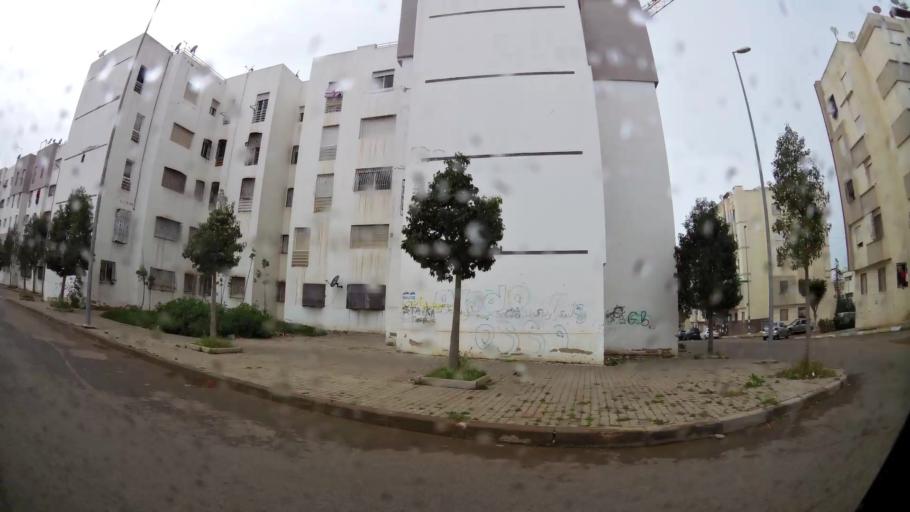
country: MA
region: Grand Casablanca
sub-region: Casablanca
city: Casablanca
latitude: 33.5473
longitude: -7.6936
